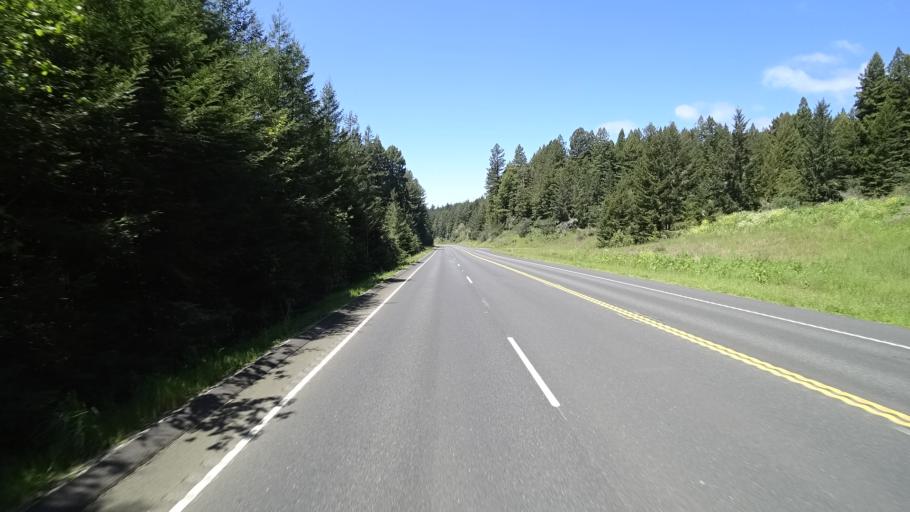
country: US
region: California
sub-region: Humboldt County
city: Blue Lake
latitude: 40.8871
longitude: -123.9738
